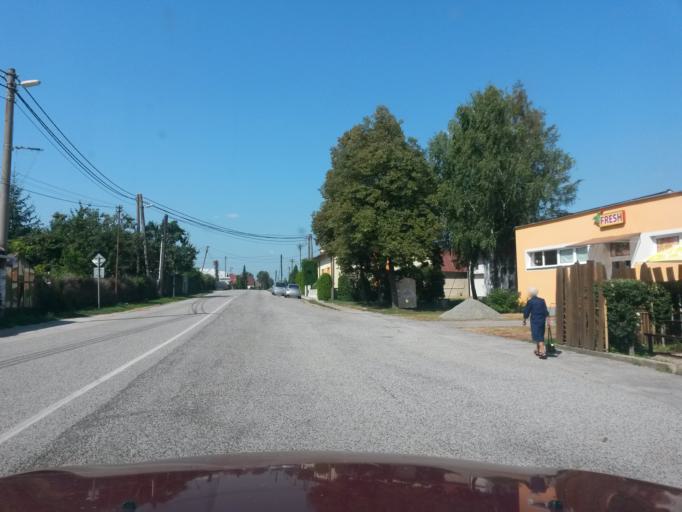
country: HU
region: Borsod-Abauj-Zemplen
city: Gonc
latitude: 48.5345
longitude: 21.1874
